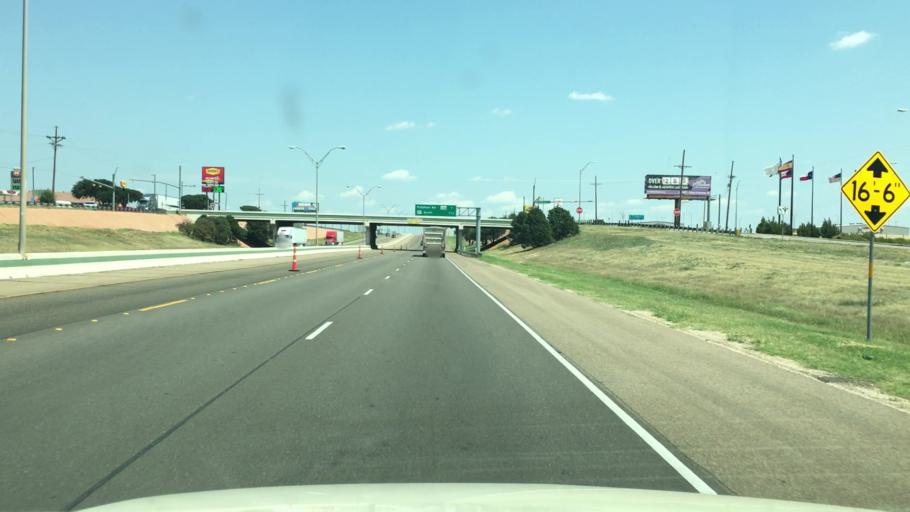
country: US
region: Texas
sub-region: Potter County
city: Amarillo
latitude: 35.1927
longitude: -101.7264
